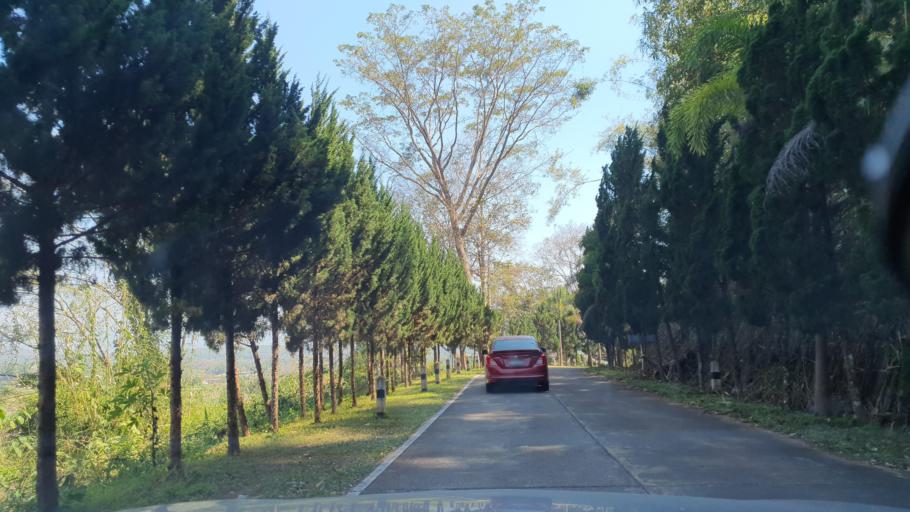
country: TH
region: Lampang
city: Wang Nuea
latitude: 19.1851
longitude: 99.4988
